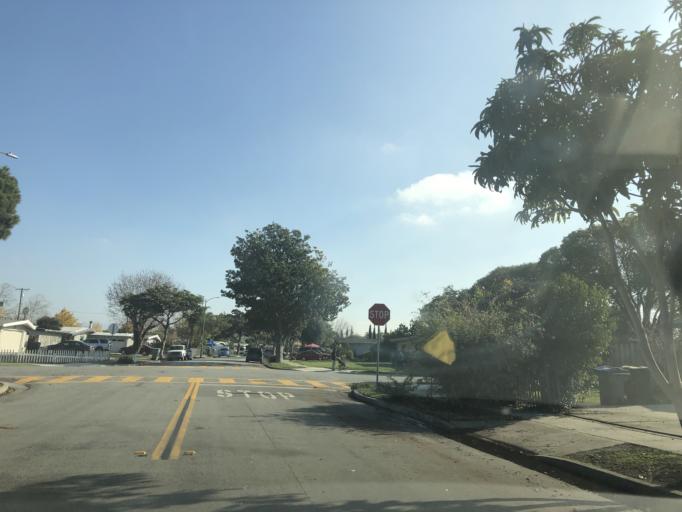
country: US
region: California
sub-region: Santa Clara County
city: Sunnyvale
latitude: 37.3946
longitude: -121.9925
